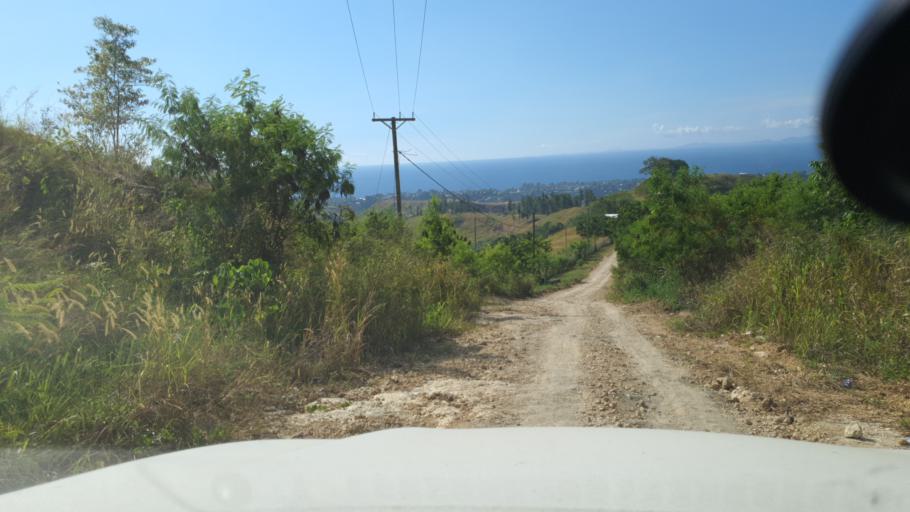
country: SB
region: Guadalcanal
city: Honiara
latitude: -9.4623
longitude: 159.9755
